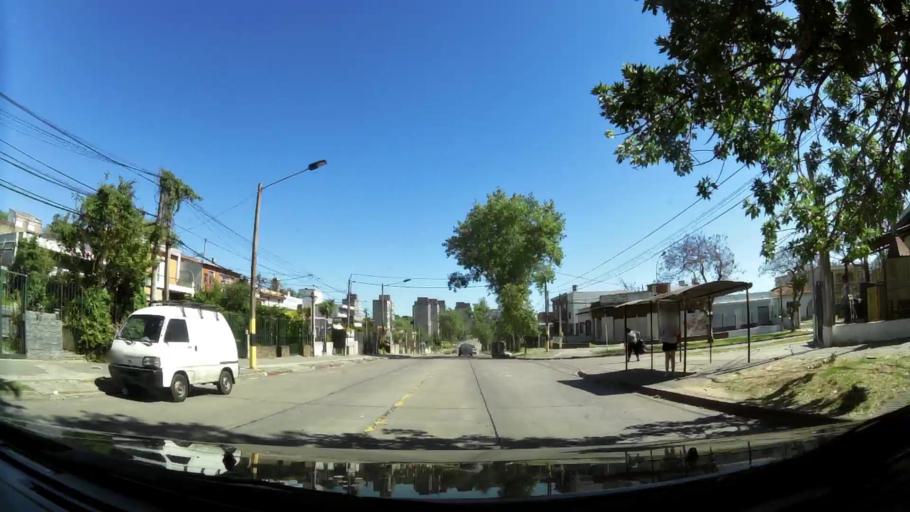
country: UY
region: Canelones
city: Paso de Carrasco
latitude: -34.8856
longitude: -56.1106
